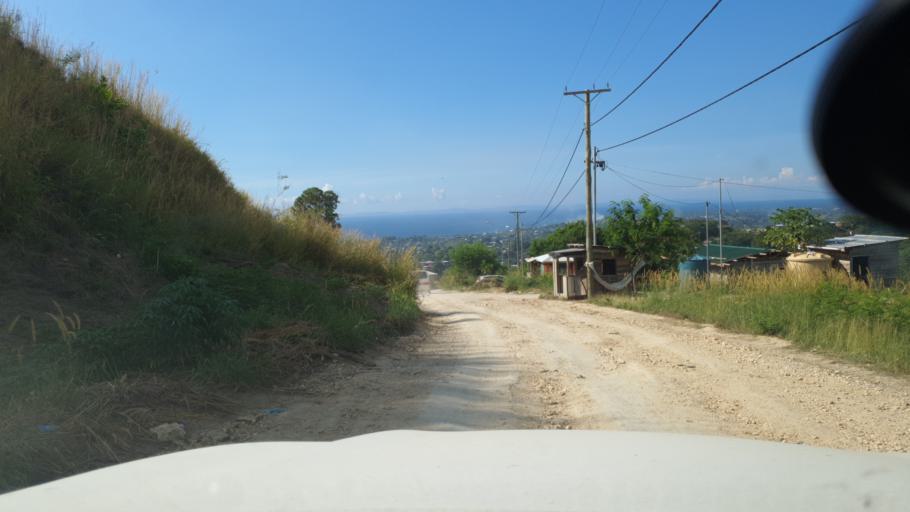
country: SB
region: Guadalcanal
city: Honiara
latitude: -9.4585
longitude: 159.9767
